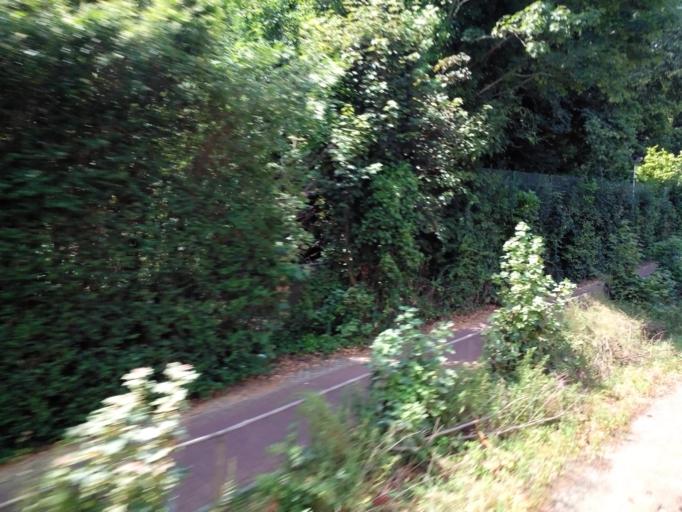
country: BE
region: Flanders
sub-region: Provincie Antwerpen
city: Boechout
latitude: 51.1613
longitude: 4.4971
